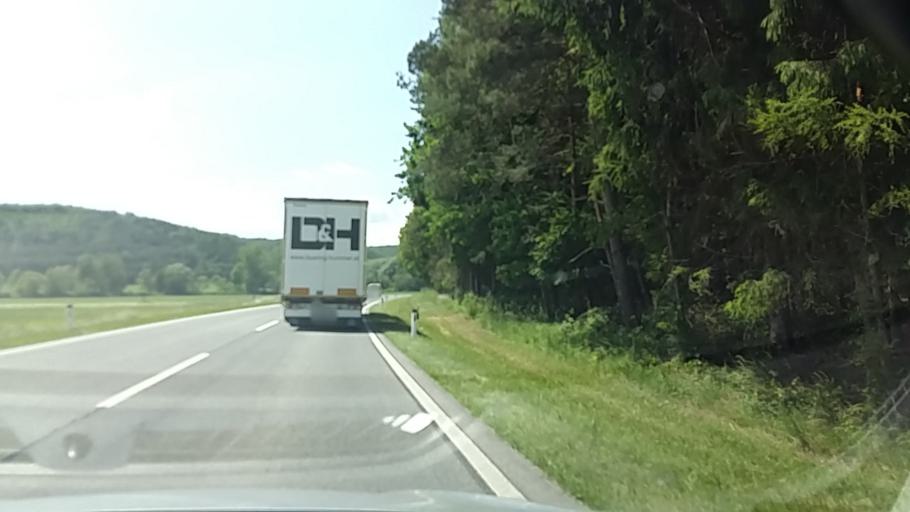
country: AT
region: Burgenland
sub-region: Politischer Bezirk Oberpullendorf
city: Piringsdorf
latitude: 47.4621
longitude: 16.4478
